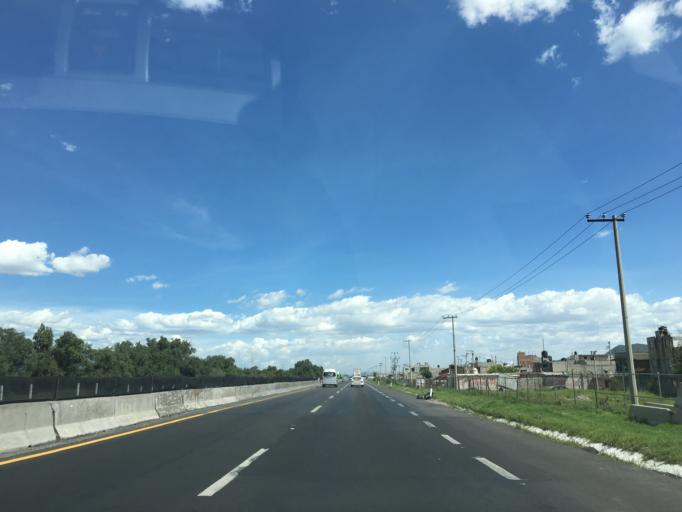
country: MX
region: Mexico
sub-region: Jaltenco
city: Alborada Jaltenco
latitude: 19.6600
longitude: -99.0637
